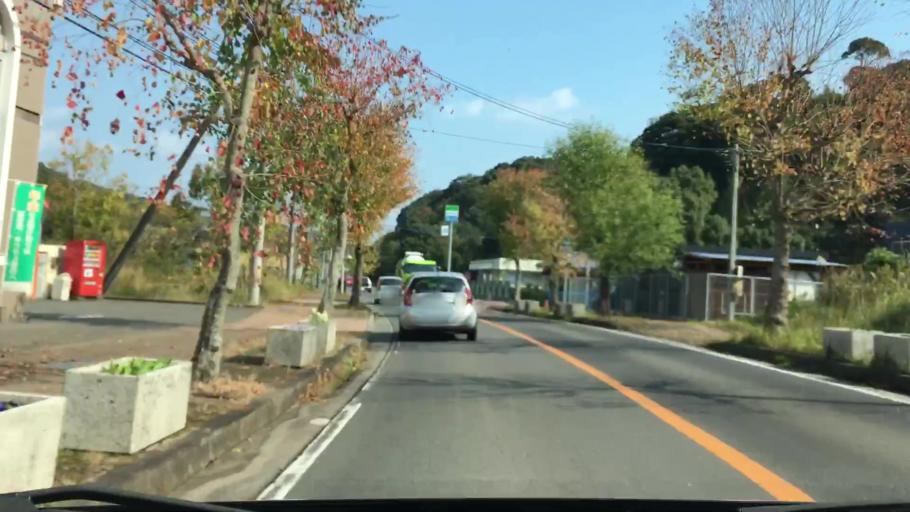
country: JP
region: Nagasaki
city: Togitsu
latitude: 32.9865
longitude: 129.7692
